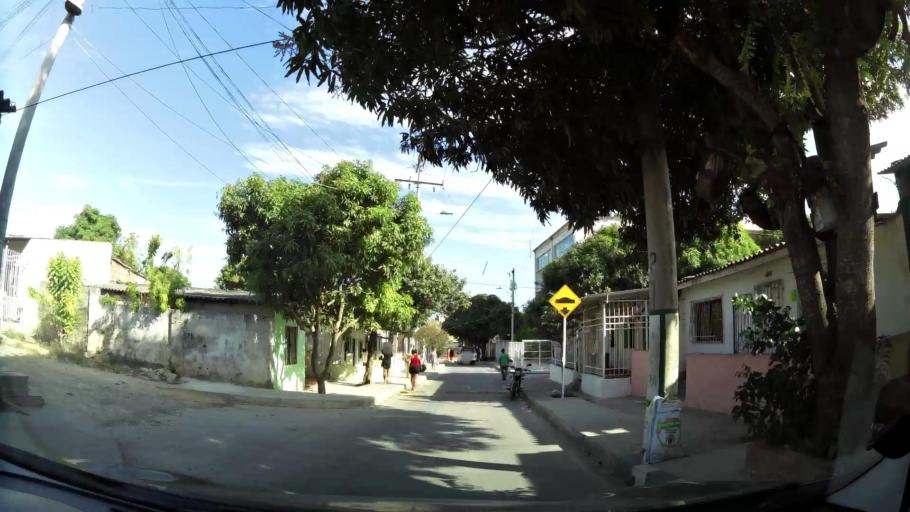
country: CO
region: Atlantico
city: Soledad
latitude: 10.9258
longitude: -74.8121
